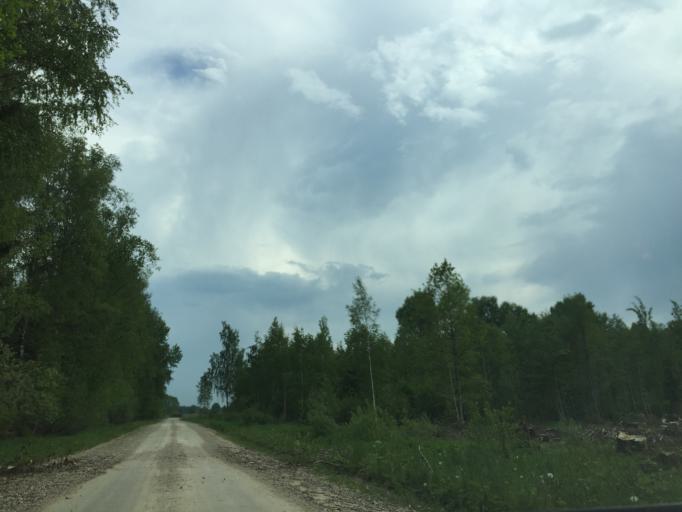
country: LV
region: Livani
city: Livani
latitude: 56.5565
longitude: 26.2245
